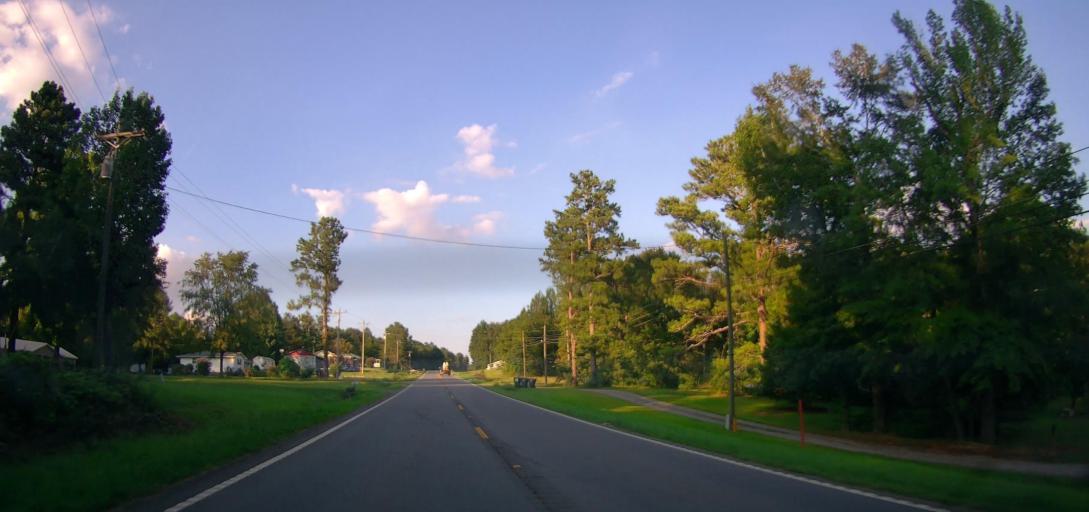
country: US
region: Georgia
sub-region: Crawford County
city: Roberta
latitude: 32.7045
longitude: -84.0349
